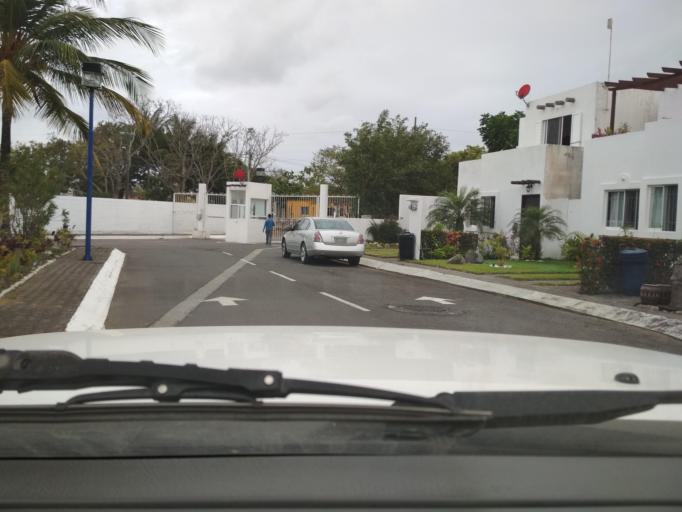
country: MX
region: Veracruz
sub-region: Medellin
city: Fraccionamiento Arboledas San Ramon
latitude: 19.0902
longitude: -96.1368
